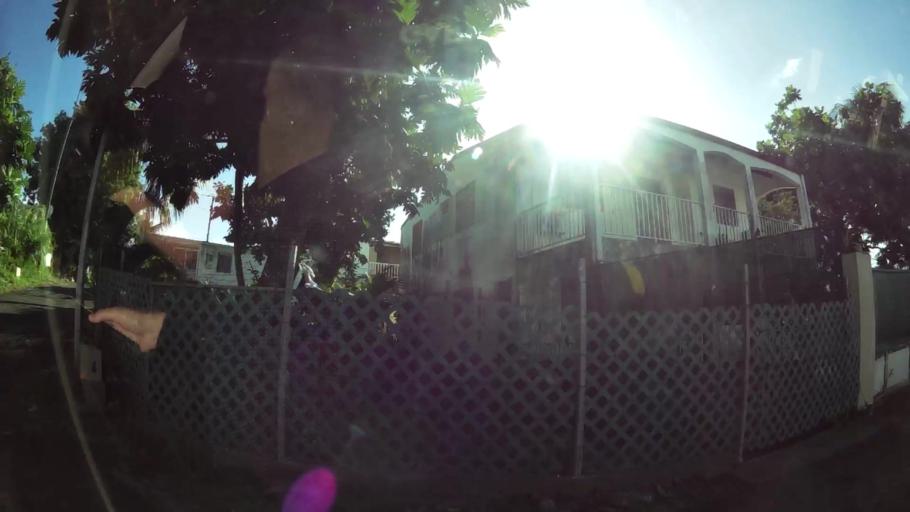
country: GP
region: Guadeloupe
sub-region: Guadeloupe
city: Le Gosier
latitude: 16.2059
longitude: -61.4815
